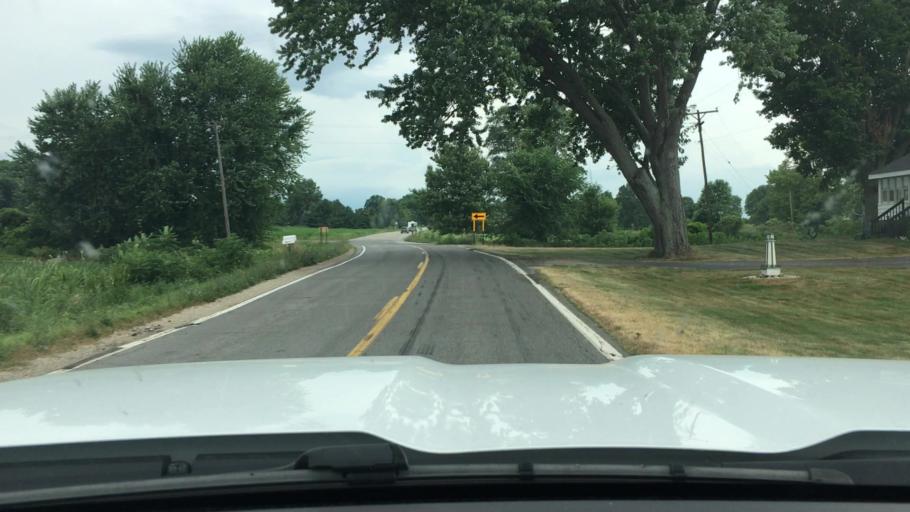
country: US
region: Michigan
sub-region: Kent County
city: Byron Center
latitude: 42.7830
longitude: -85.7811
